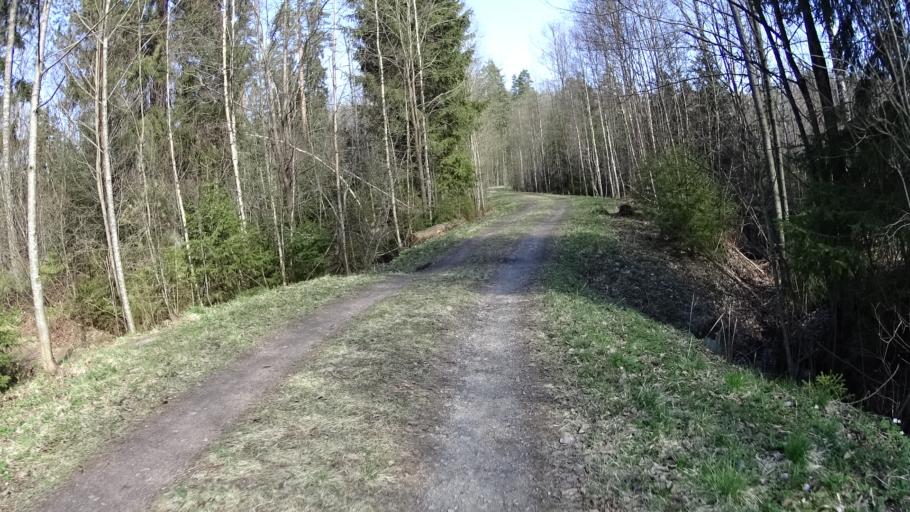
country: FI
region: Uusimaa
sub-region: Helsinki
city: Espoo
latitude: 60.2457
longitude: 24.6233
